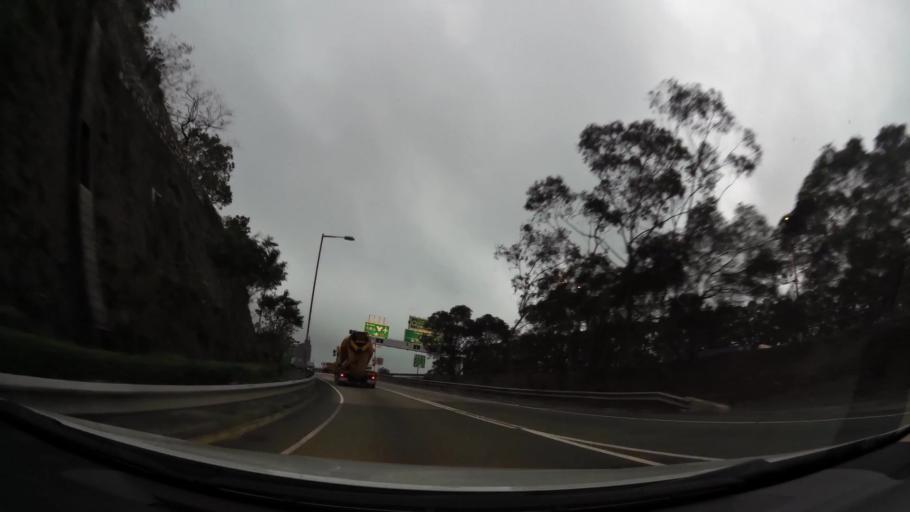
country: HK
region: Tsuen Wan
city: Tsuen Wan
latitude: 22.3584
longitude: 114.0832
